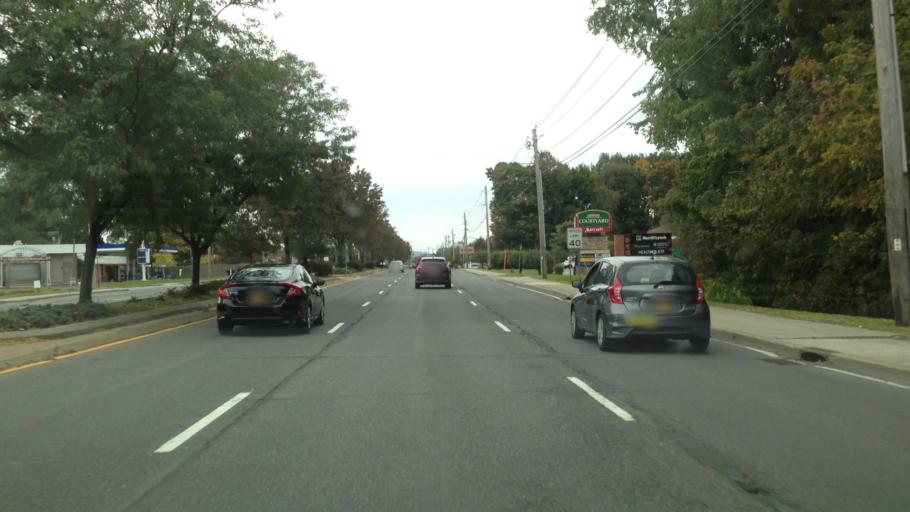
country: US
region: New York
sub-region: Dutchess County
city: Spackenkill
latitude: 41.6712
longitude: -73.9292
